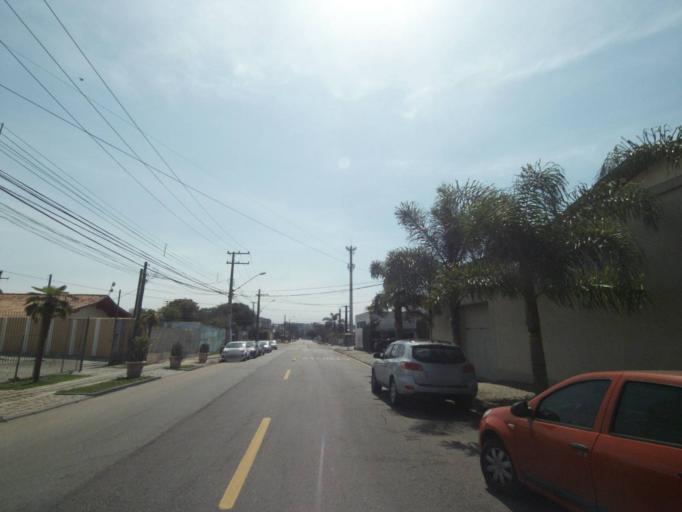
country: BR
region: Parana
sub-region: Curitiba
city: Curitiba
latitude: -25.4691
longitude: -49.3050
